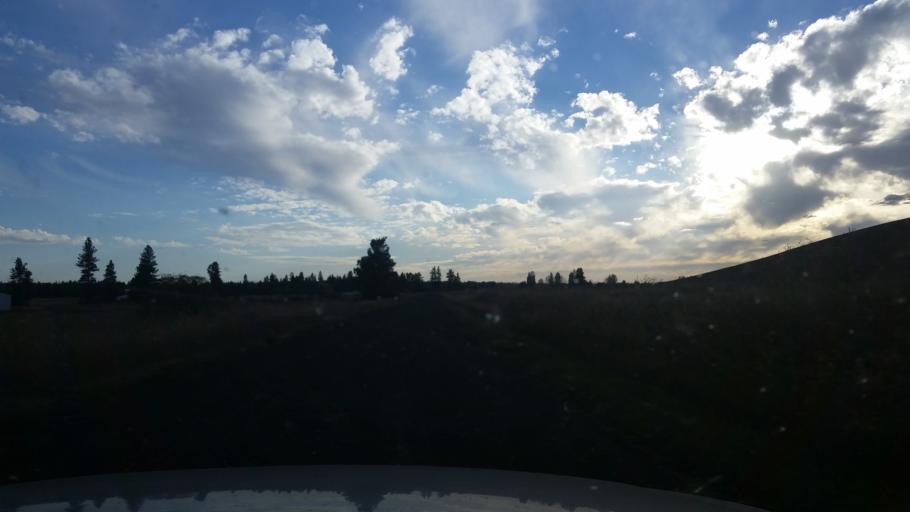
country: US
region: Washington
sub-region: Spokane County
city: Cheney
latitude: 47.4716
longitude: -117.6201
